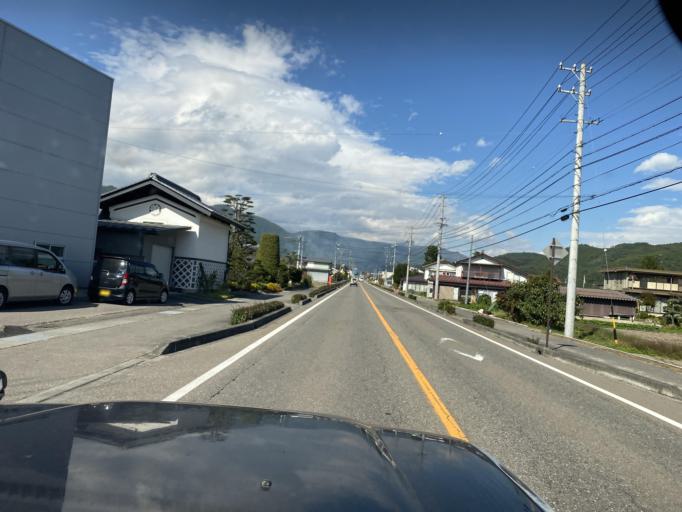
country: JP
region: Nagano
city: Omachi
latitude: 36.5250
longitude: 137.8508
